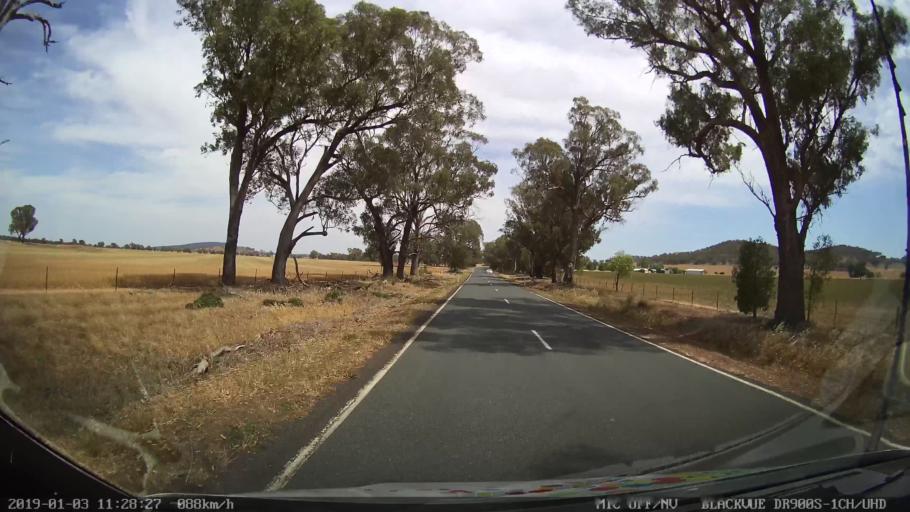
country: AU
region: New South Wales
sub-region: Weddin
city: Grenfell
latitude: -34.0021
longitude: 148.2087
